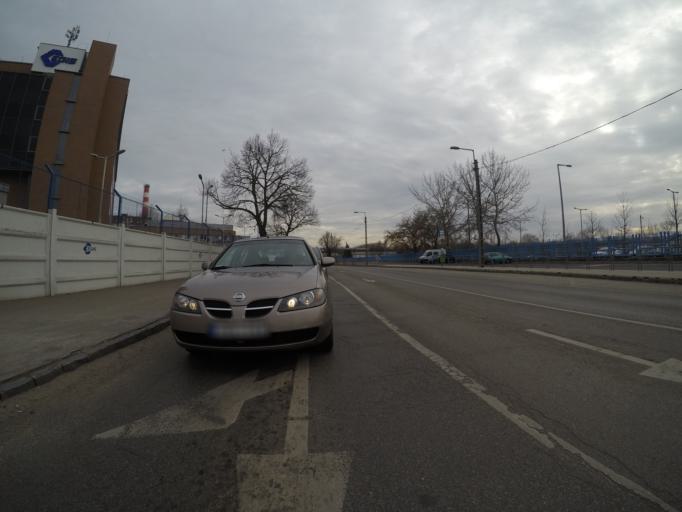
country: HU
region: Budapest
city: Budapest X. keruelet
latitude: 47.4991
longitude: 19.1540
